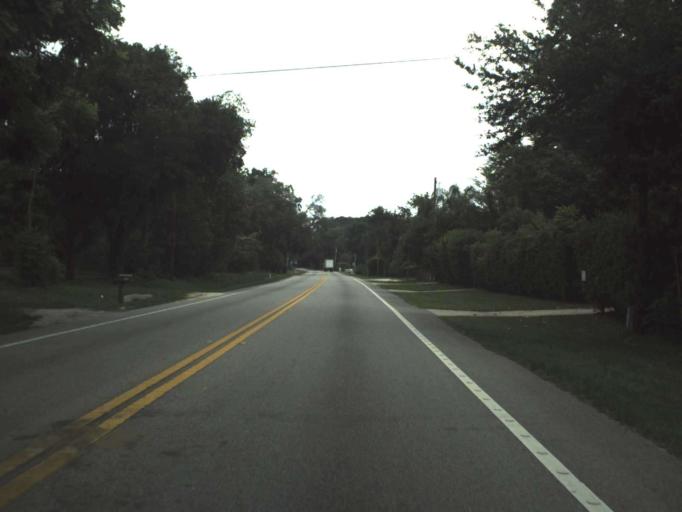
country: US
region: Florida
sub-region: Volusia County
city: Lake Helen
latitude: 29.0196
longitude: -81.2520
